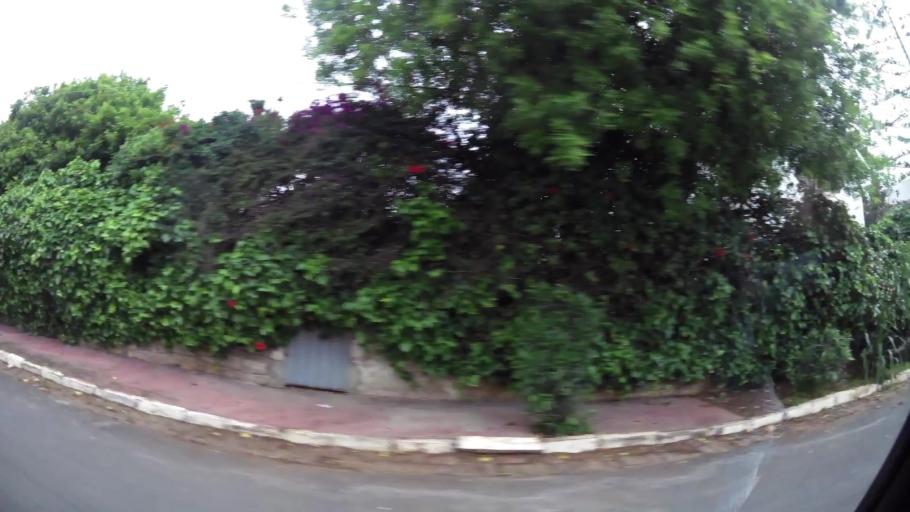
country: MA
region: Grand Casablanca
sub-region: Casablanca
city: Casablanca
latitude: 33.5772
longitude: -7.6632
